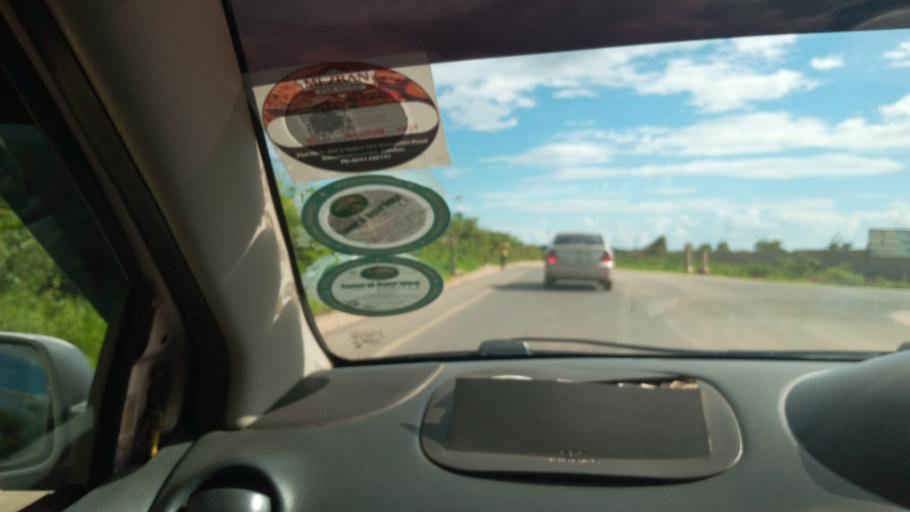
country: ZM
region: Lusaka
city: Lusaka
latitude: -15.5155
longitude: 28.3420
